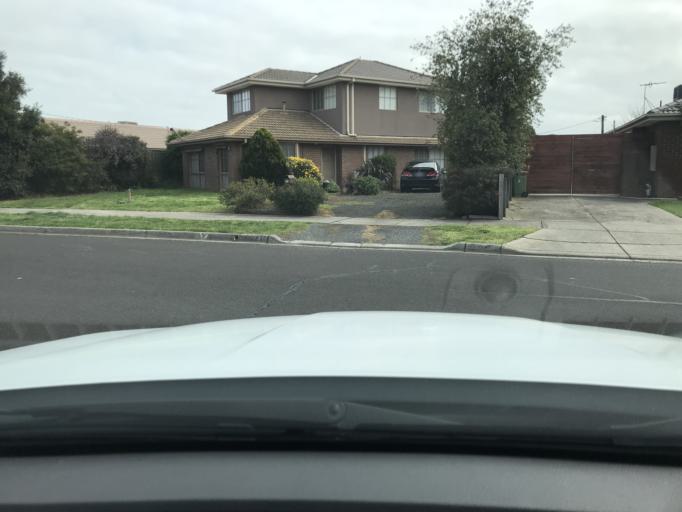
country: AU
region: Victoria
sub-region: Hume
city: Roxburgh Park
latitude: -37.6035
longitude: 144.9262
